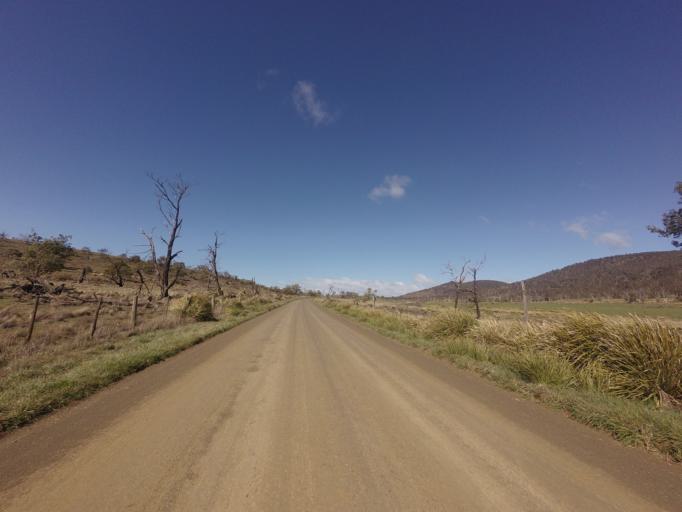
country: AU
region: Tasmania
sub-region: Northern Midlands
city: Evandale
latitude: -41.9327
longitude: 147.4173
